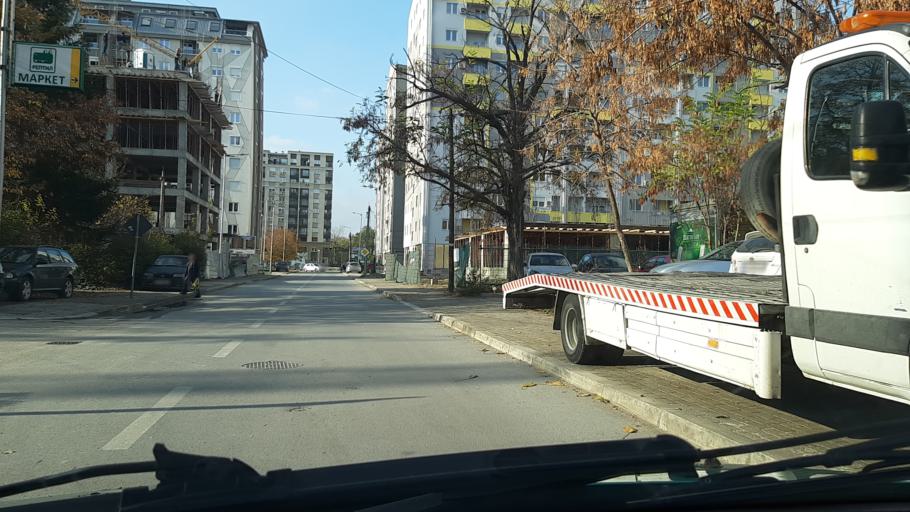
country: MK
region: Karpos
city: Skopje
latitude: 41.9846
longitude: 21.4533
